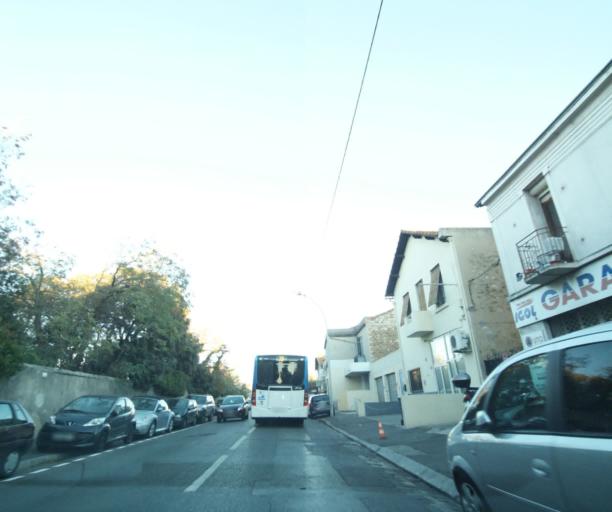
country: FR
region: Provence-Alpes-Cote d'Azur
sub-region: Departement des Bouches-du-Rhone
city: Marseille 12
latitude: 43.3080
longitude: 5.4327
